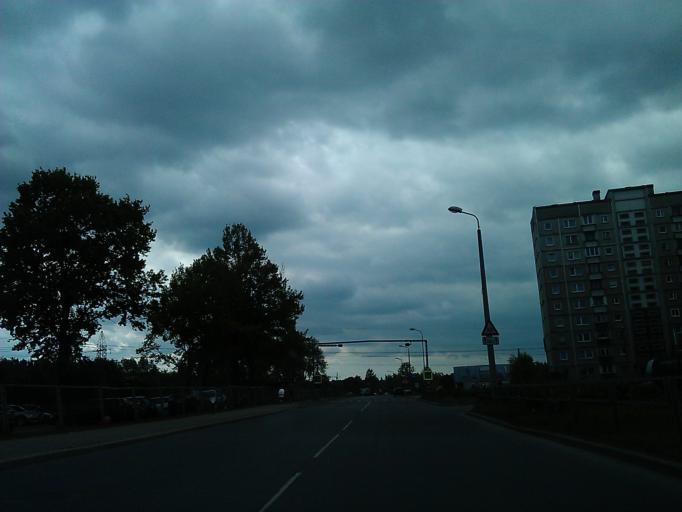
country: LV
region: Kekava
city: Balozi
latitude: 56.8999
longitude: 24.0926
